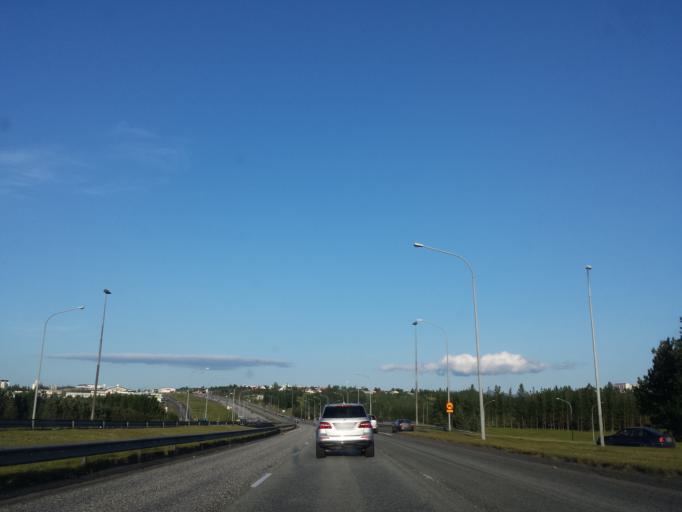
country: IS
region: Capital Region
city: Reykjavik
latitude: 64.1253
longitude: -21.8509
